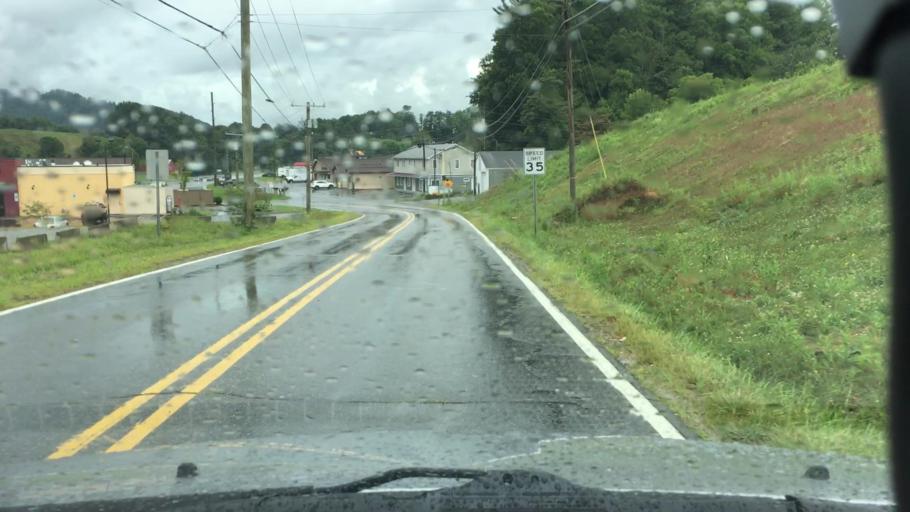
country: US
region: North Carolina
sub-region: Yancey County
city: Burnsville
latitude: 35.9136
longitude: -82.3132
